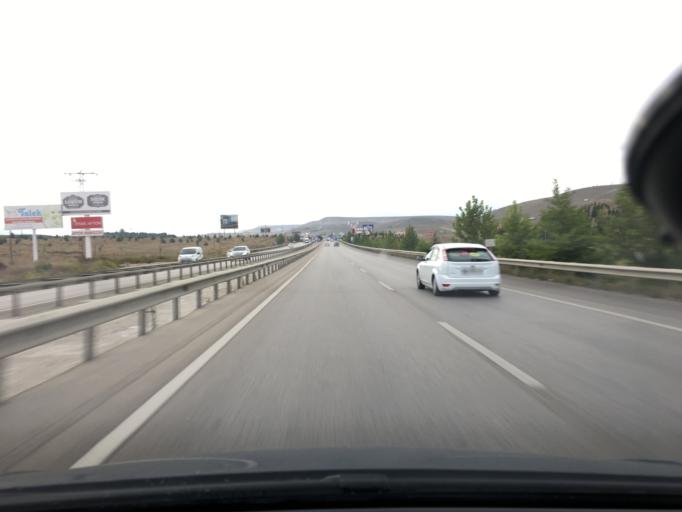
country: TR
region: Afyonkarahisar
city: Afyonkarahisar
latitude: 38.7930
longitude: 30.4100
